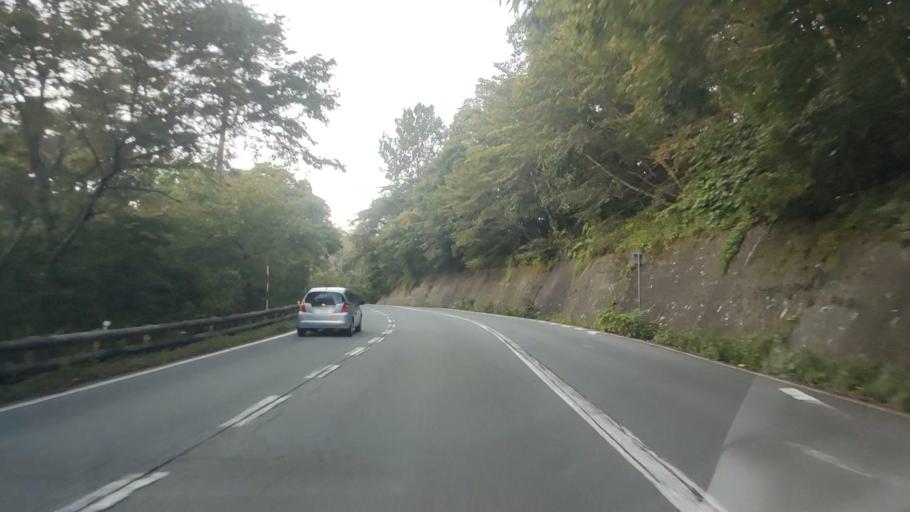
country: JP
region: Nagano
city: Komoro
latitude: 36.3834
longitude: 138.5882
